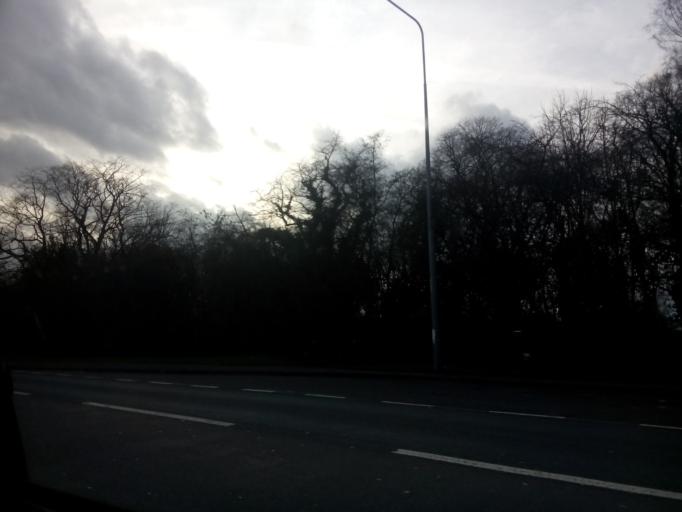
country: GB
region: England
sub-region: Worcestershire
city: Bromsgrove
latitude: 52.3570
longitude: -2.0461
